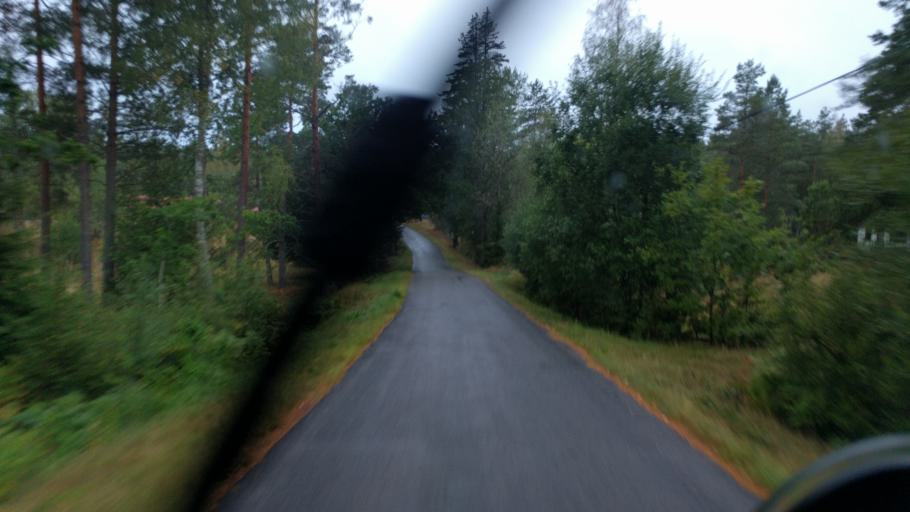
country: SE
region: Kalmar
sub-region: Vasterviks Kommun
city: Ankarsrum
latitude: 57.8260
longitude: 16.2774
